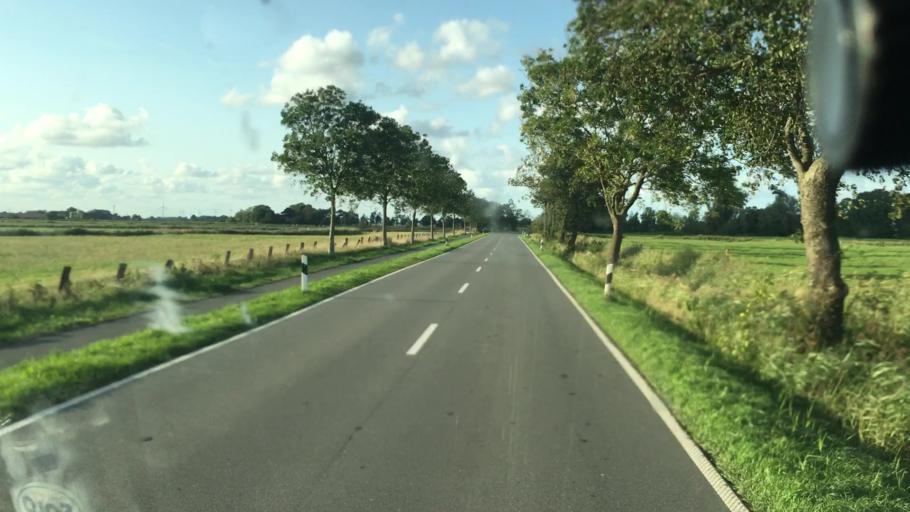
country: DE
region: Lower Saxony
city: Jever
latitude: 53.6019
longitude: 7.8697
